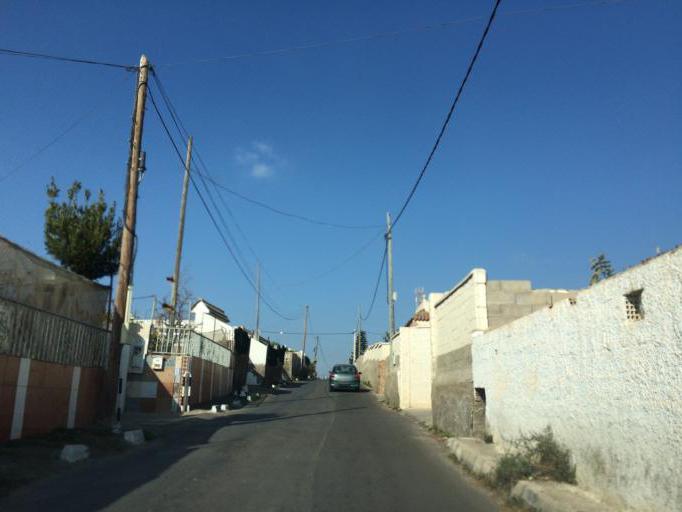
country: ES
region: Andalusia
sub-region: Provincia de Almeria
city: Viator
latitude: 36.8658
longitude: -2.4184
